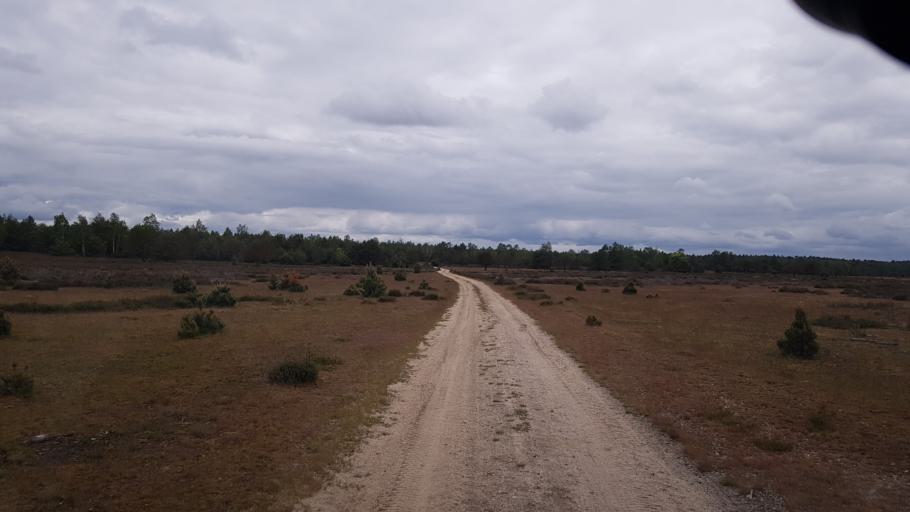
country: DE
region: Brandenburg
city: Hohenleipisch
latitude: 51.5121
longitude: 13.5072
